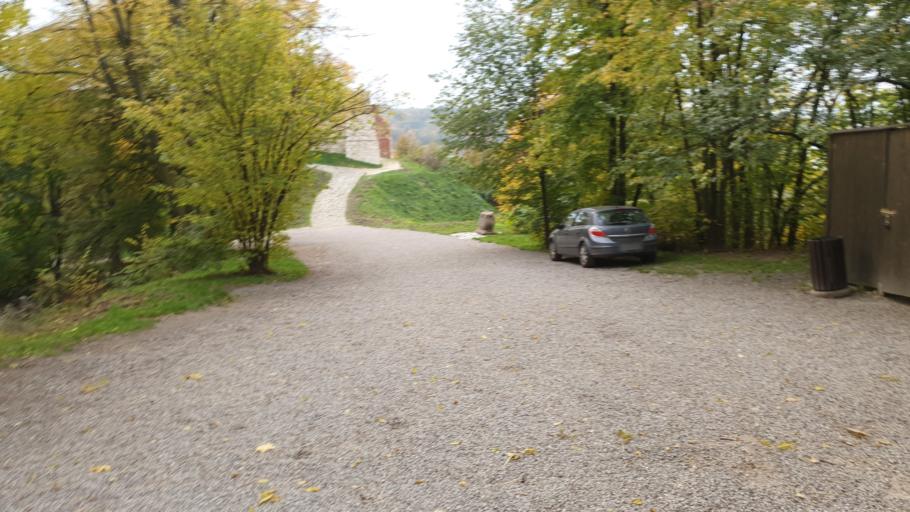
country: PL
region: Lublin Voivodeship
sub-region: Powiat pulawski
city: Kazimierz Dolny
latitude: 51.3243
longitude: 21.9514
